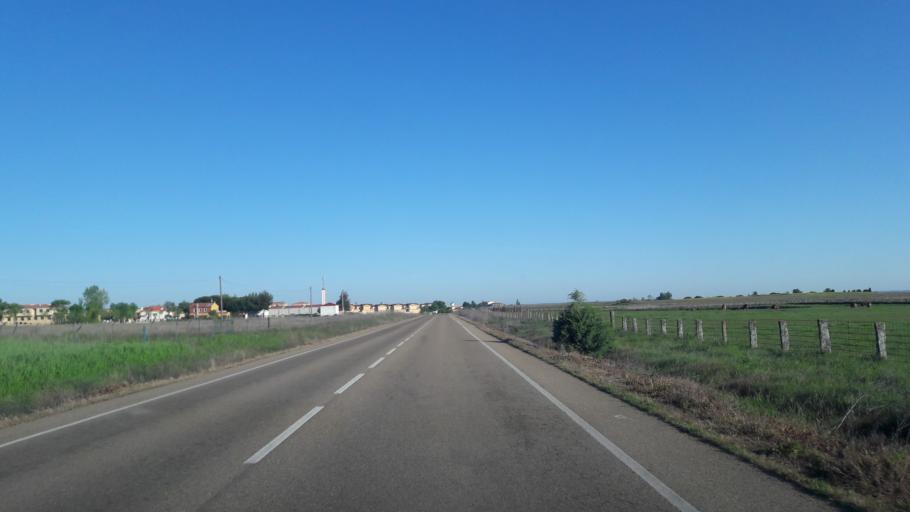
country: ES
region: Castille and Leon
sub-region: Provincia de Salamanca
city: La Fuente de San Esteban
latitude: 40.7960
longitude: -6.2486
